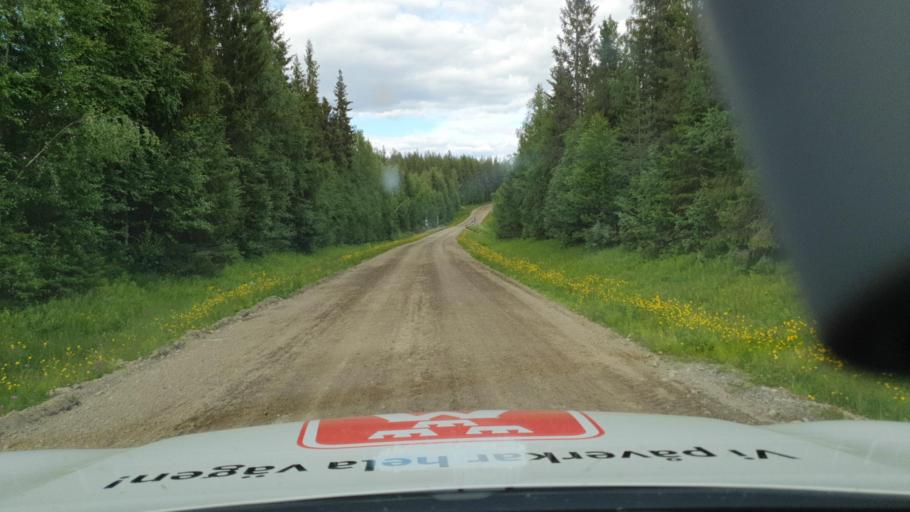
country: SE
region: Vaesterbotten
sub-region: Lycksele Kommun
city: Lycksele
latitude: 64.3338
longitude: 18.4254
